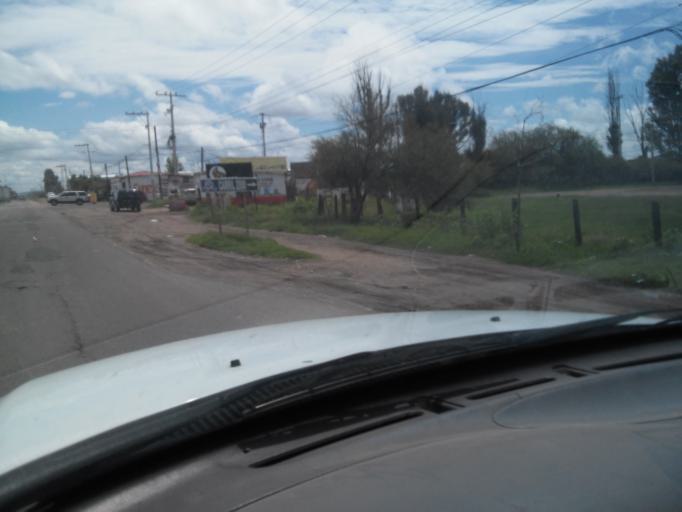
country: MX
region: Durango
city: Victoria de Durango
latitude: 24.0281
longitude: -104.5924
